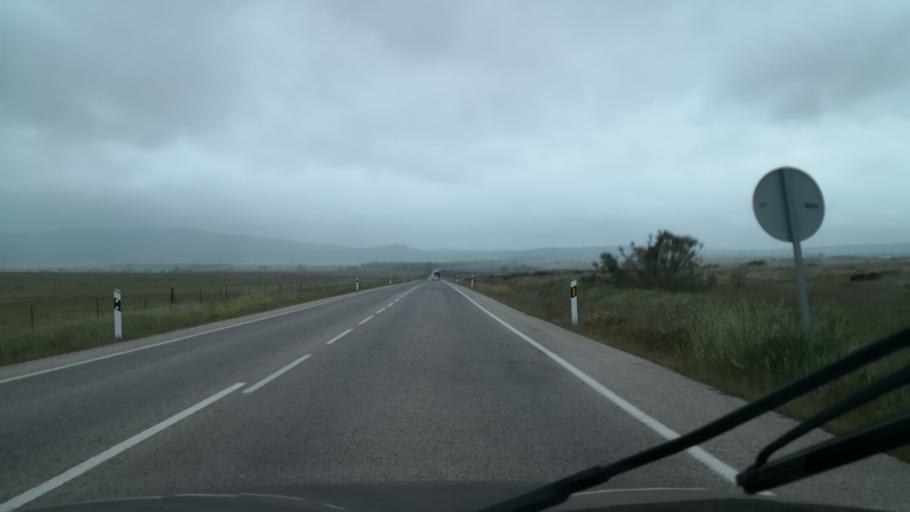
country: ES
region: Extremadura
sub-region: Provincia de Caceres
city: Malpartida de Caceres
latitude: 39.3452
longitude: -6.4734
